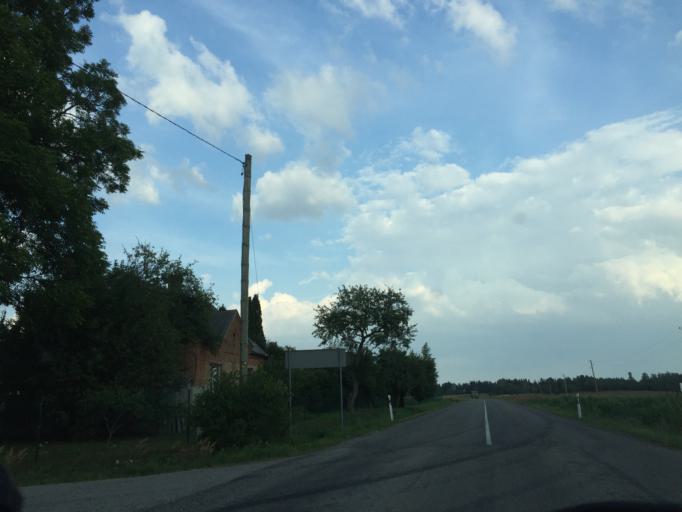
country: LV
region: Dobeles Rajons
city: Dobele
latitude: 56.5967
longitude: 23.3178
